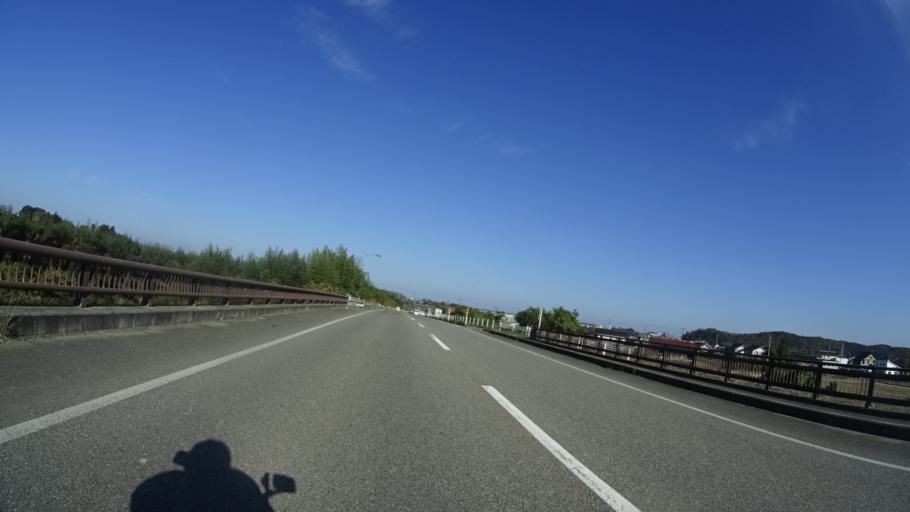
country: JP
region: Ishikawa
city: Komatsu
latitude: 36.3029
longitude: 136.3861
